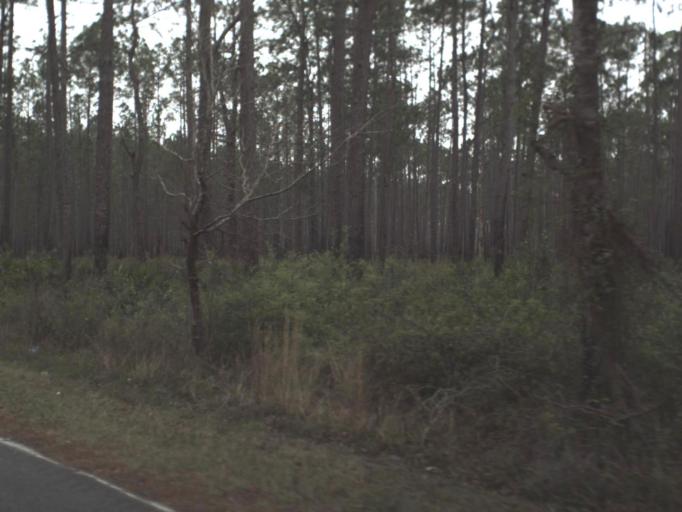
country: US
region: Florida
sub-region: Franklin County
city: Apalachicola
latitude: 29.9635
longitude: -84.9760
